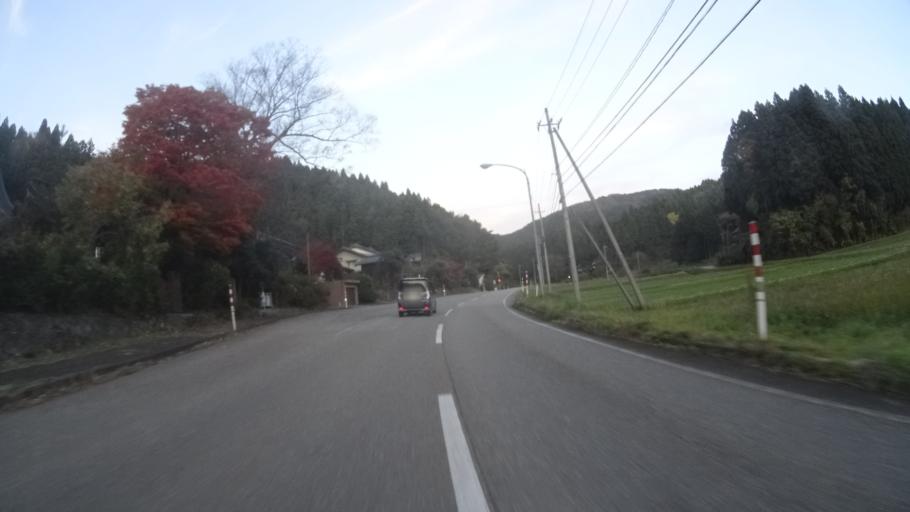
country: JP
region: Ishikawa
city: Nanao
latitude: 37.3130
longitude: 136.7994
